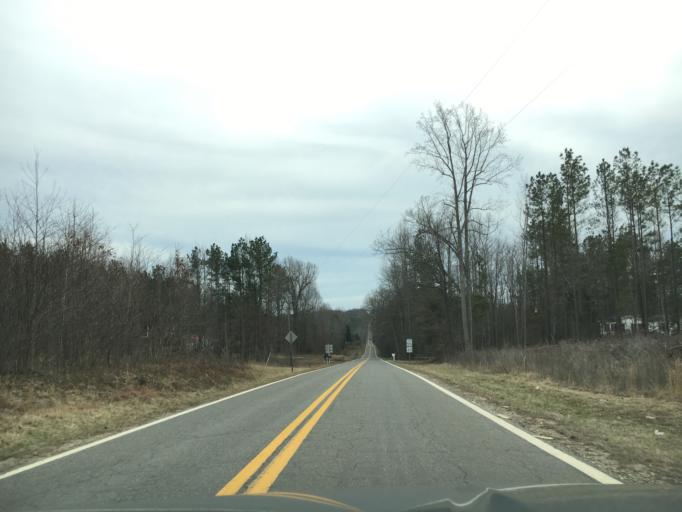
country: US
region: Virginia
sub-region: Charlotte County
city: Charlotte Court House
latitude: 37.0739
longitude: -78.7237
